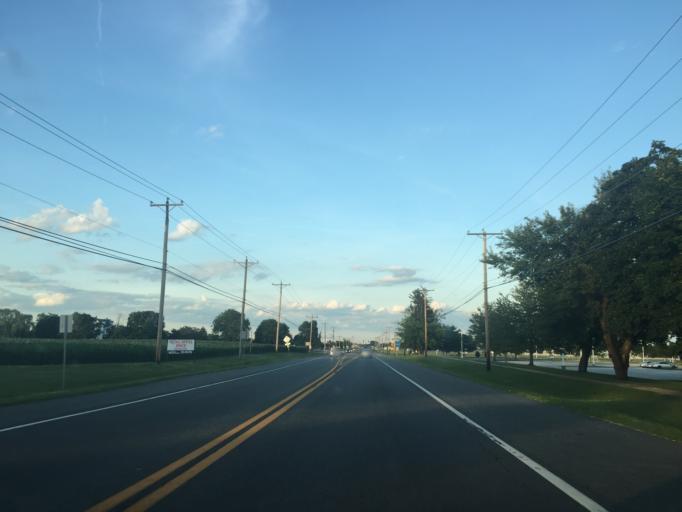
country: US
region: Delaware
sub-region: New Castle County
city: Middletown
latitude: 39.4510
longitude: -75.6947
